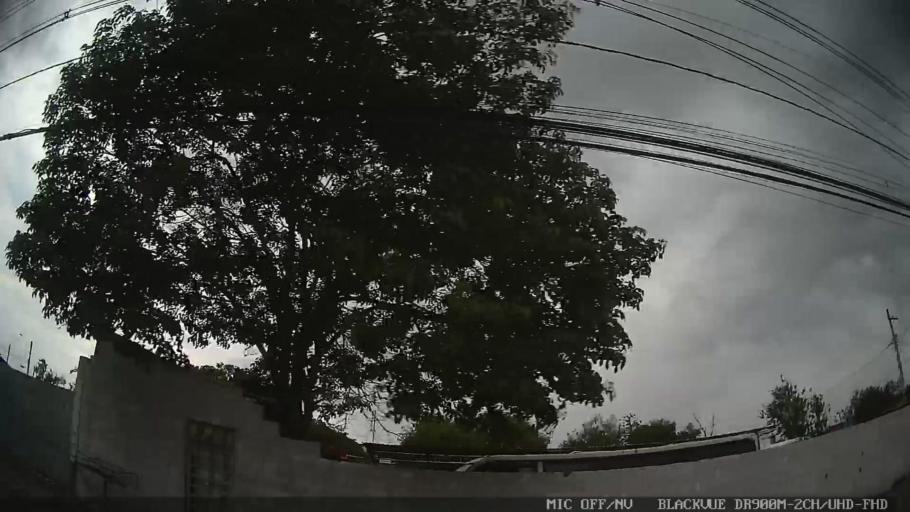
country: BR
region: Sao Paulo
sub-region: Amparo
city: Amparo
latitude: -22.7106
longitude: -46.8145
